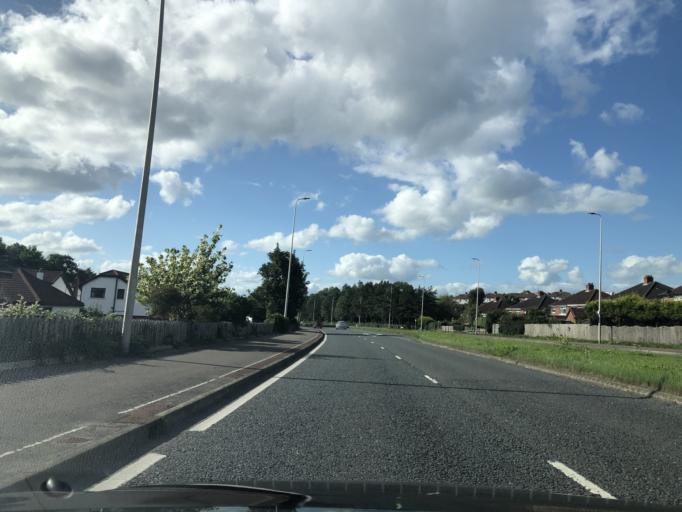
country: GB
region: Northern Ireland
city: Holywood
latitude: 54.6120
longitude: -5.8574
